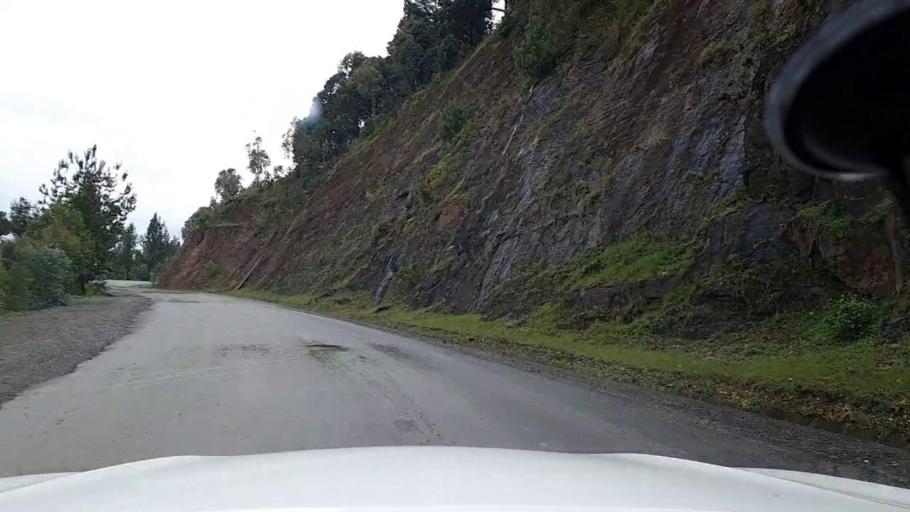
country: RW
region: Western Province
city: Kibuye
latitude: -2.0672
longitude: 29.5437
